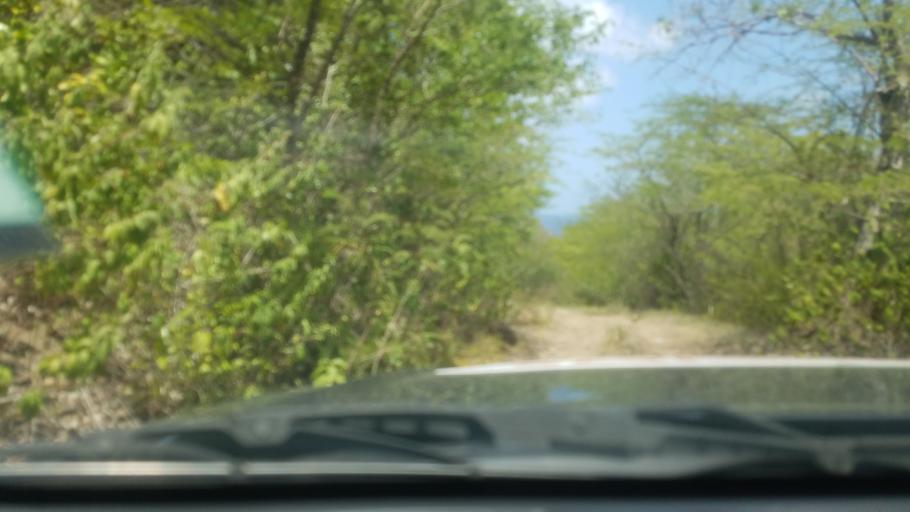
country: LC
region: Vieux-Fort
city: Vieux Fort
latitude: 13.7124
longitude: -60.9550
